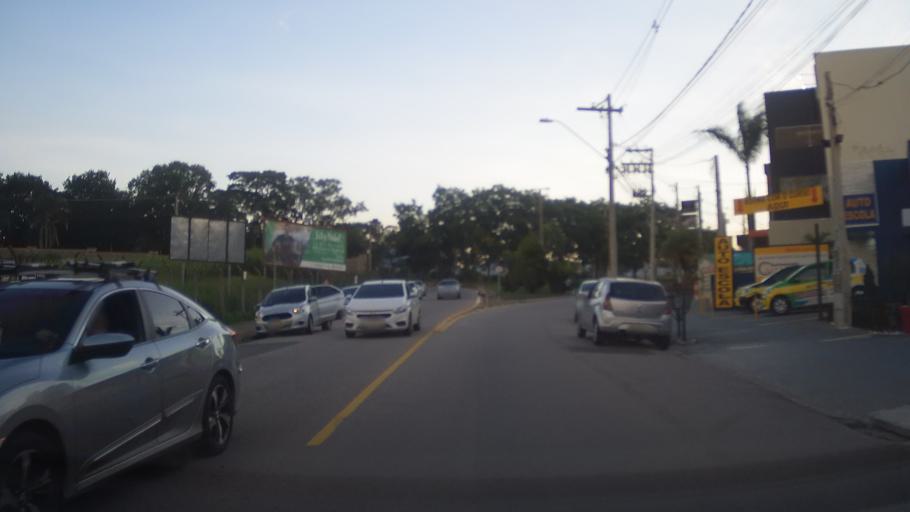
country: BR
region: Sao Paulo
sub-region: Jundiai
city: Jundiai
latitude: -23.1921
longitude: -46.9610
